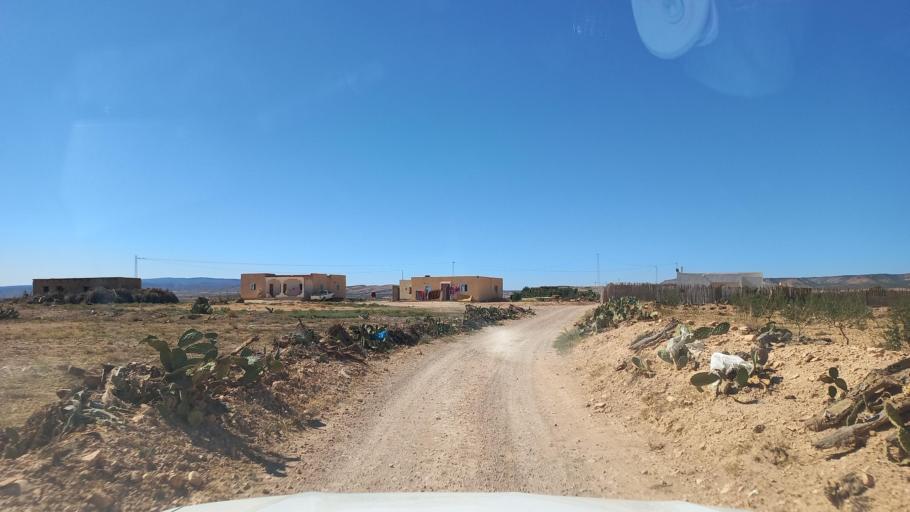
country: TN
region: Al Qasrayn
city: Sbiba
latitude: 35.3777
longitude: 9.0763
